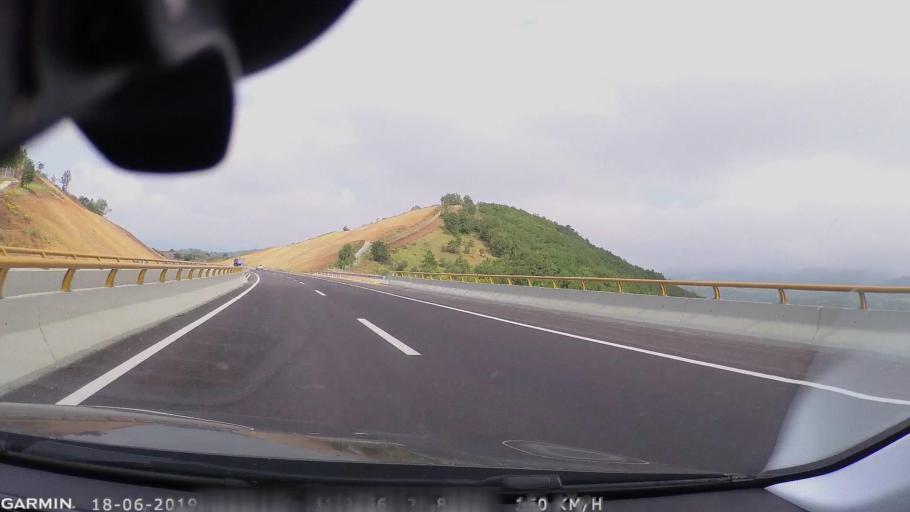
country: MK
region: Sveti Nikole
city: Gorobinci
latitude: 41.9216
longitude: 21.8640
